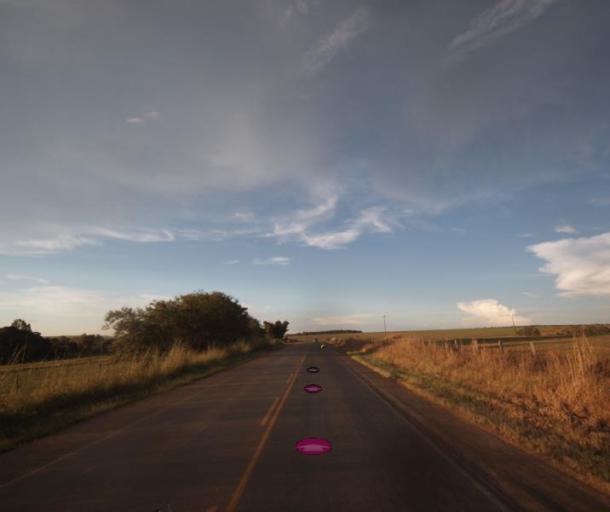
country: BR
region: Goias
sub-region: Anapolis
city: Anapolis
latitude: -16.1857
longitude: -48.9037
